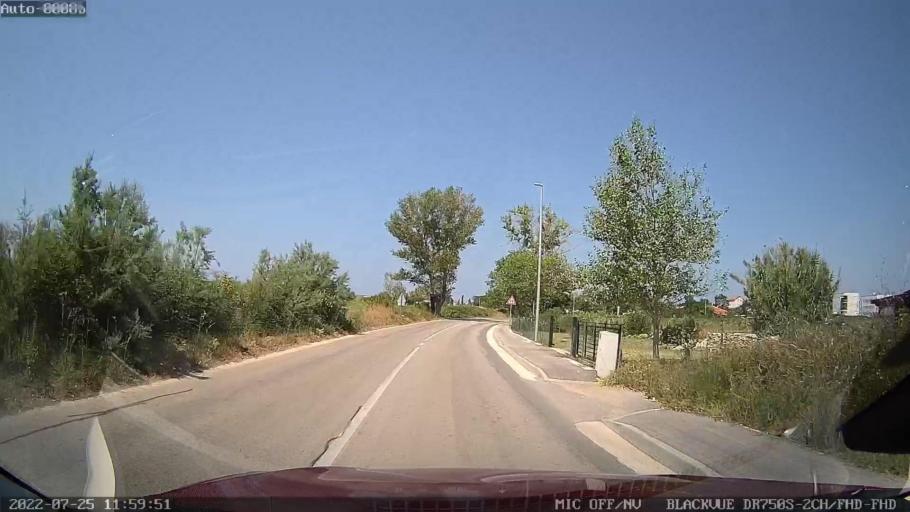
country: HR
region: Zadarska
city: Nin
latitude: 44.2424
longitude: 15.1977
